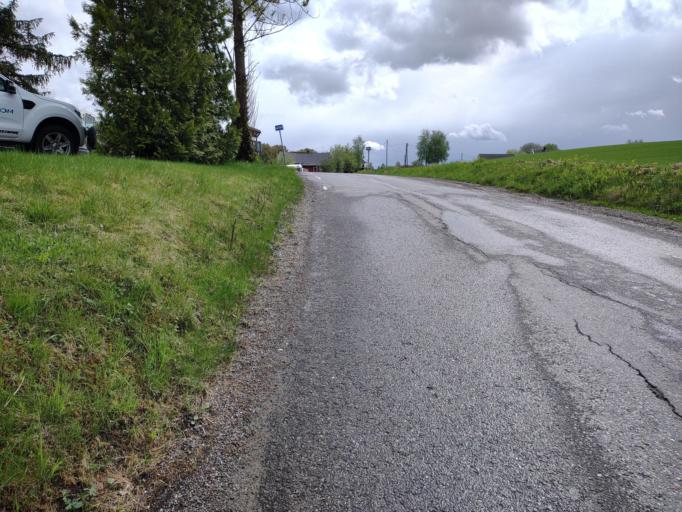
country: NO
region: Akershus
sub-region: Nannestad
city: Teigebyen
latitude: 60.2444
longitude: 10.9896
